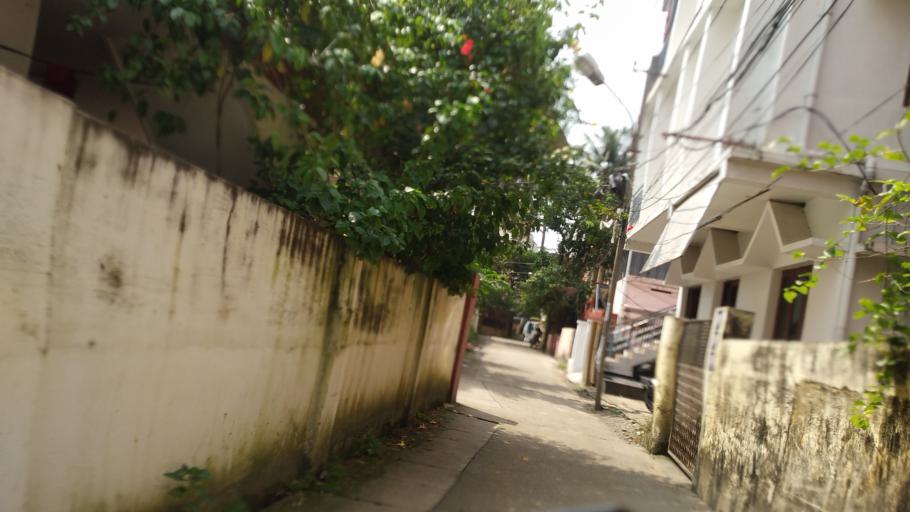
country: IN
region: Kerala
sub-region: Ernakulam
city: Cochin
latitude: 9.9692
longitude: 76.3031
